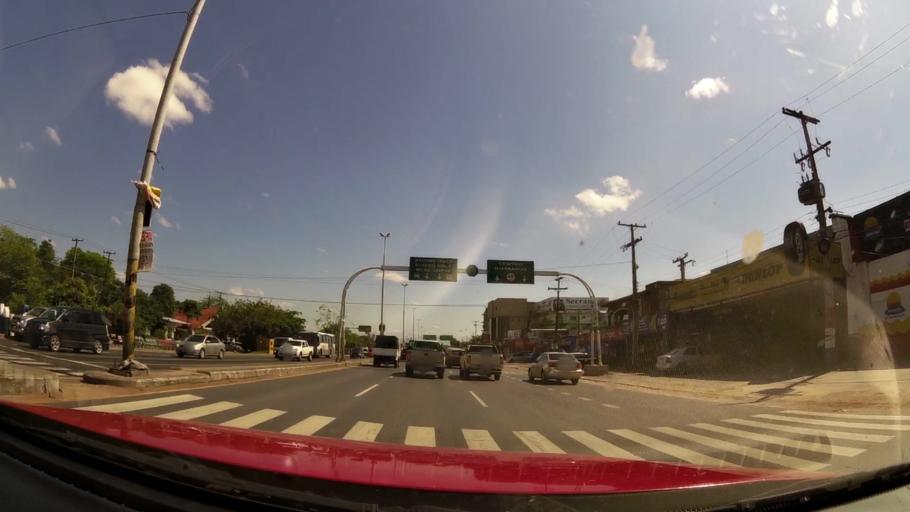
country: PY
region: Central
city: Colonia Mariano Roque Alonso
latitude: -25.2432
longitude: -57.5459
